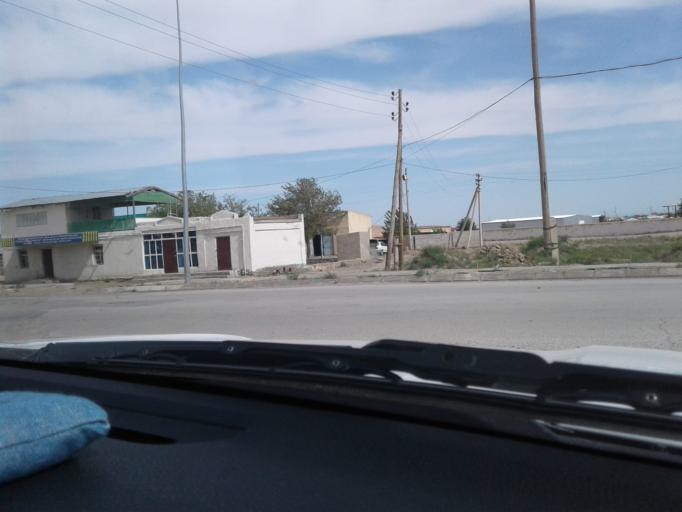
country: TM
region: Balkan
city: Gazanjyk
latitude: 39.2450
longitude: 55.5039
